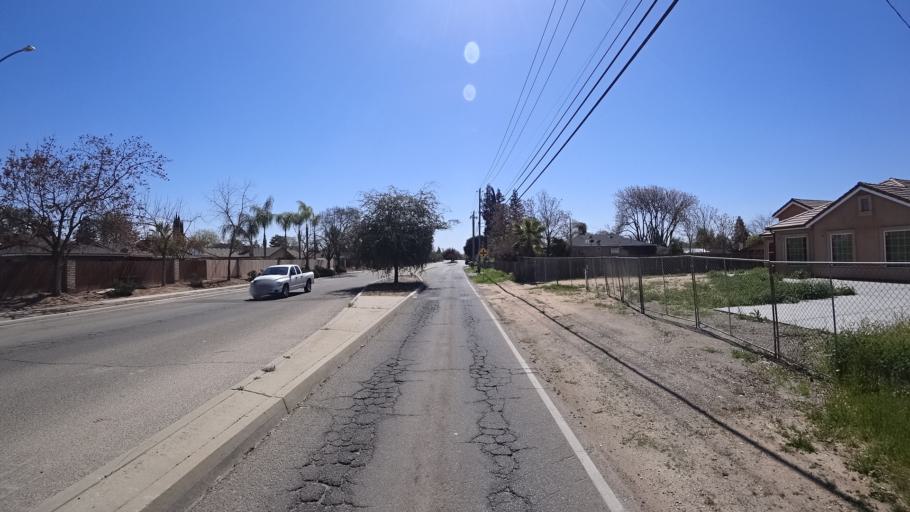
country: US
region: California
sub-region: Fresno County
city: West Park
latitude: 36.7765
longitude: -119.8713
